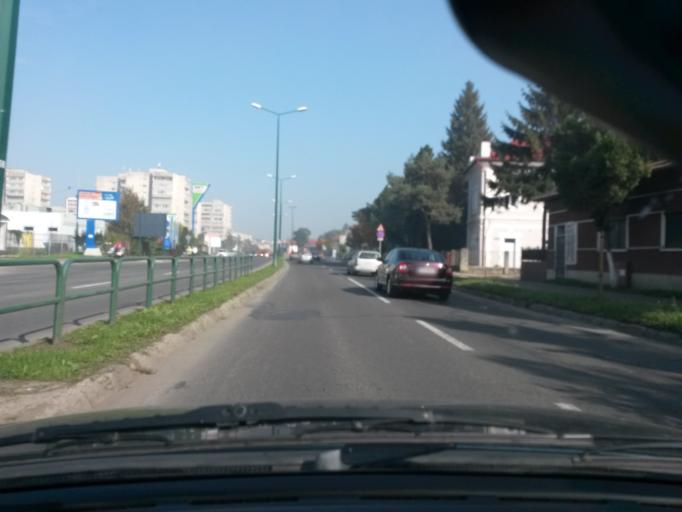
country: RO
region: Mures
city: Targu-Mures
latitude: 46.5304
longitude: 24.5488
